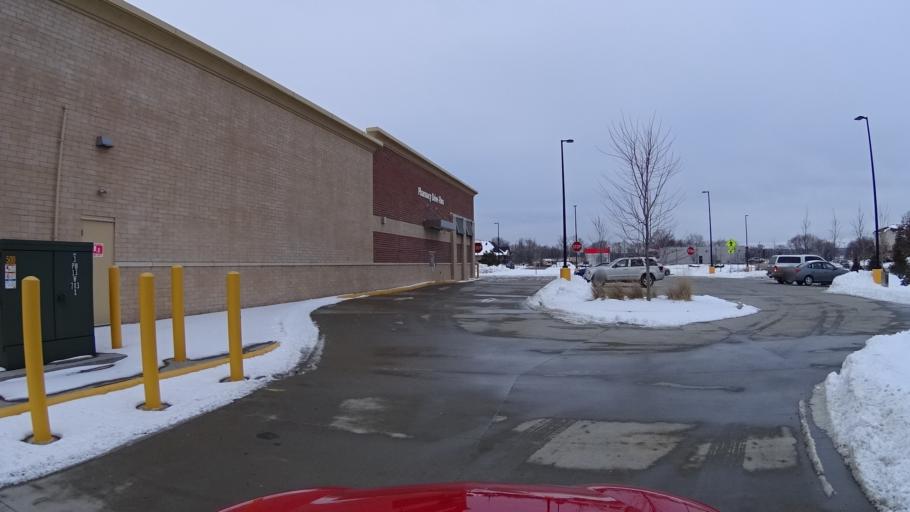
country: US
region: Nebraska
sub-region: Sarpy County
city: Offutt Air Force Base
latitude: 41.1161
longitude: -95.9424
